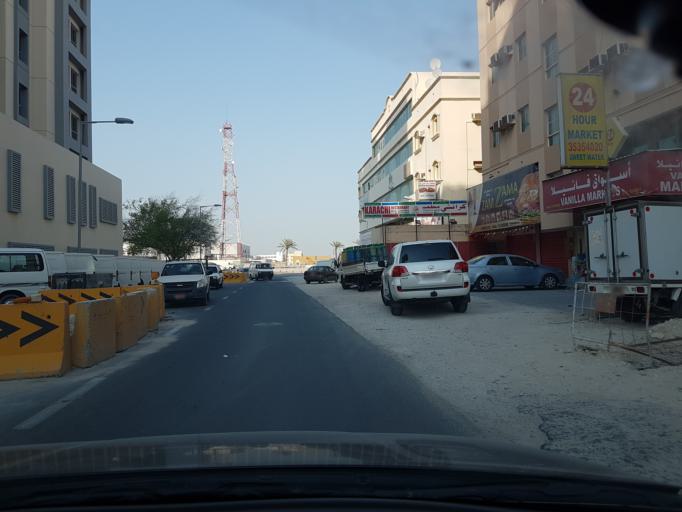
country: BH
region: Northern
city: Ar Rifa'
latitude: 26.1329
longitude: 50.5840
